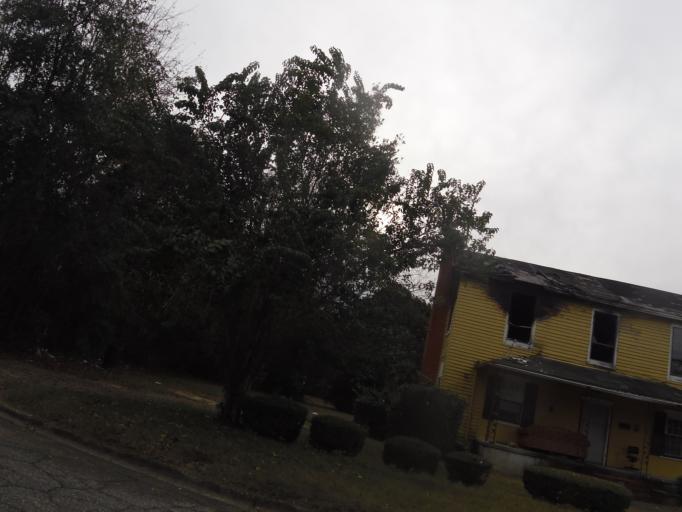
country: US
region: Georgia
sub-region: Thomas County
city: Thomasville
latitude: 30.8411
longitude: -83.9870
